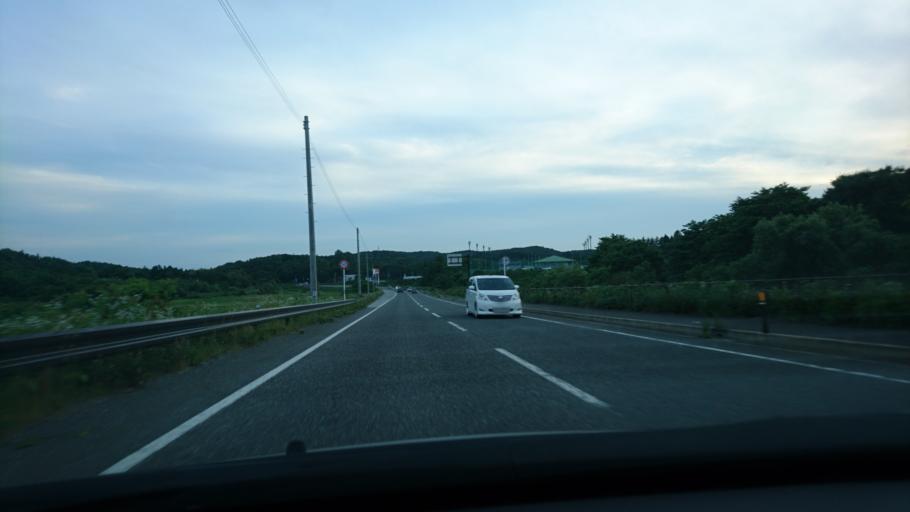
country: JP
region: Miyagi
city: Furukawa
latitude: 38.7252
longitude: 141.0292
